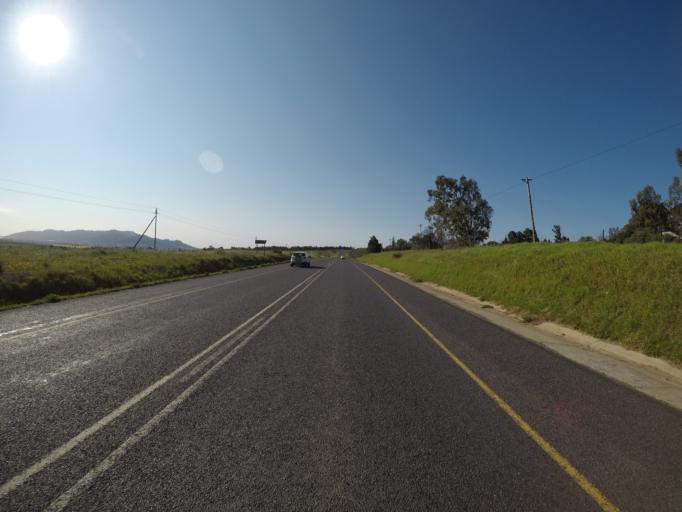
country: ZA
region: Western Cape
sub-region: Cape Winelands District Municipality
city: Noorder-Paarl
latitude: -33.6886
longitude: 18.9007
